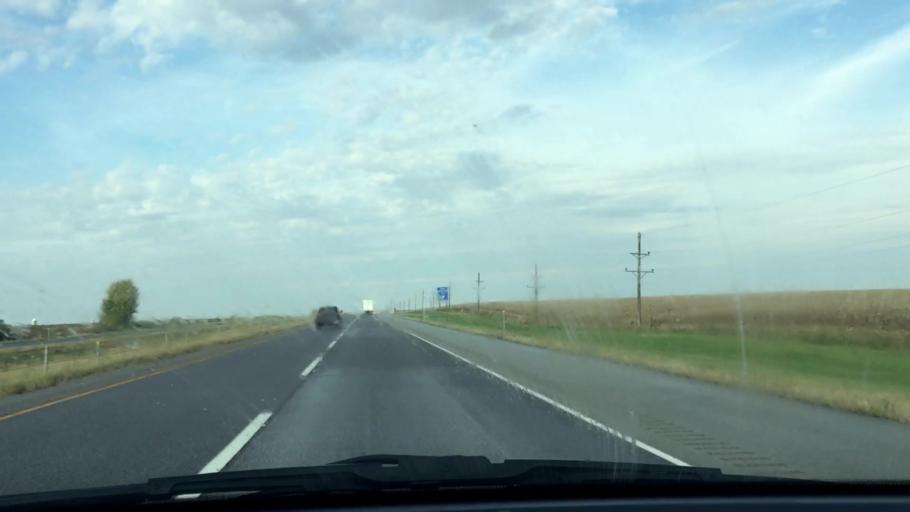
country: US
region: Illinois
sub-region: Lee County
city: Franklin Grove
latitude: 41.8229
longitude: -89.3492
